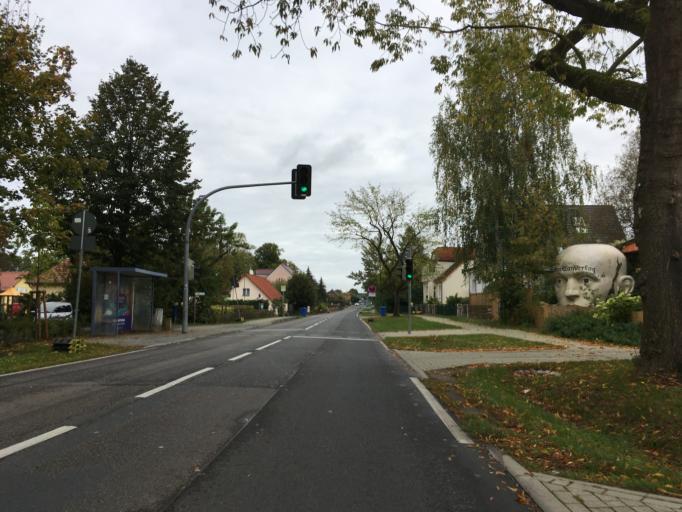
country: DE
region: Brandenburg
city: Werftpfuhl
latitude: 52.6821
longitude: 13.8393
